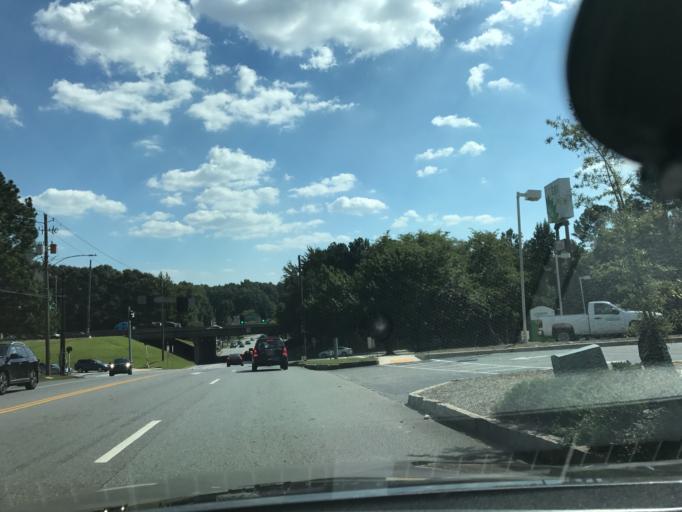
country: US
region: Georgia
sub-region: DeKalb County
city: Doraville
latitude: 33.9214
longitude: -84.2967
